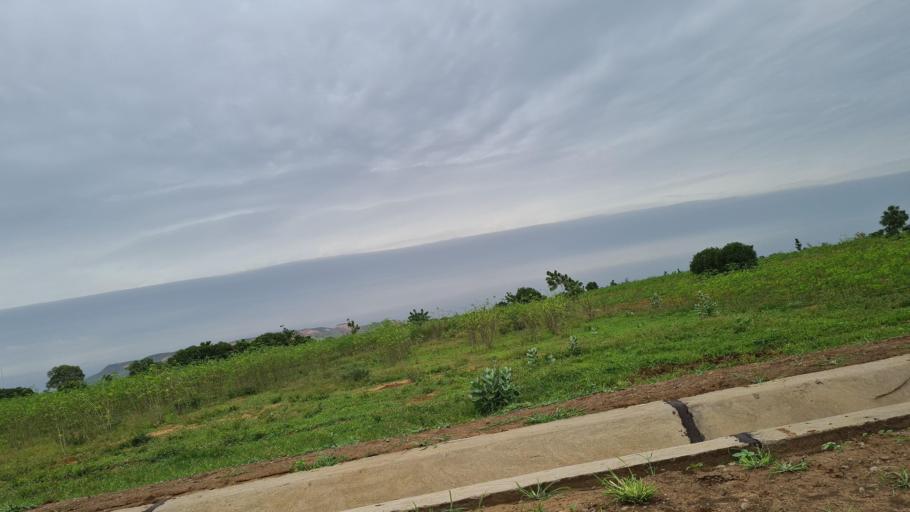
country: NE
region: Tahoua
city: Birni N Konni
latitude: 13.8328
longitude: 5.2660
